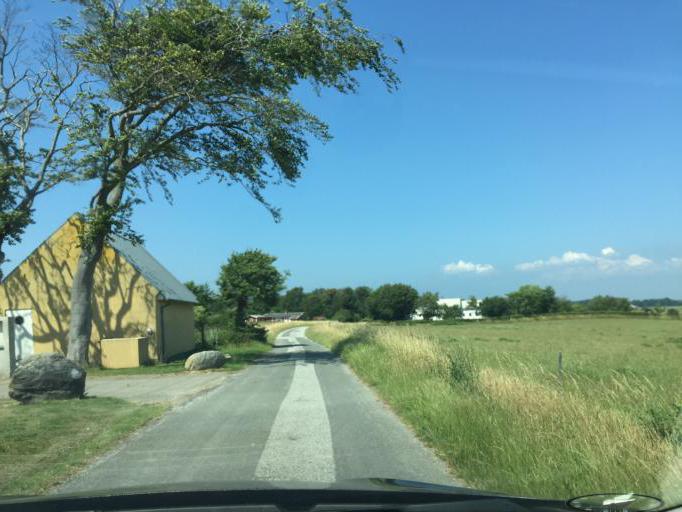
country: DK
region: Zealand
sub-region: Slagelse Kommune
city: Korsor
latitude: 55.2303
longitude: 11.1764
